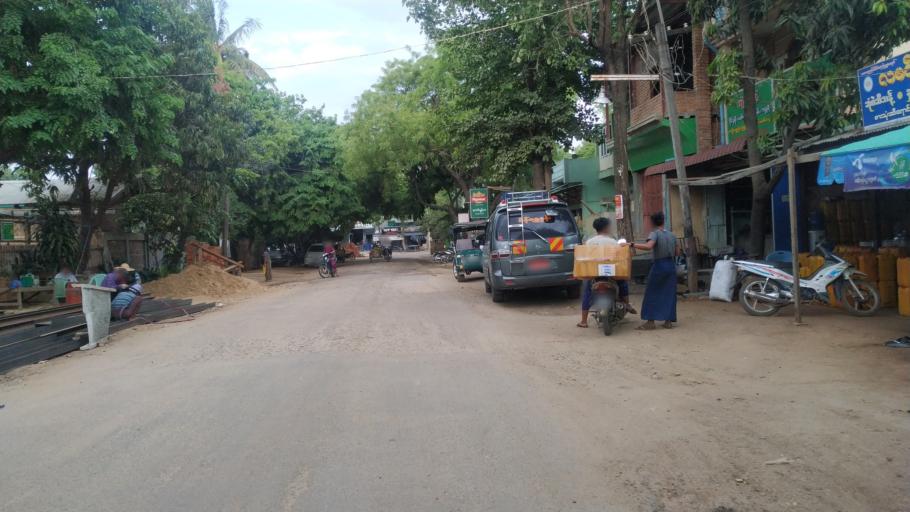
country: MM
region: Magway
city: Pakokku
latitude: 21.3357
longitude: 95.0774
